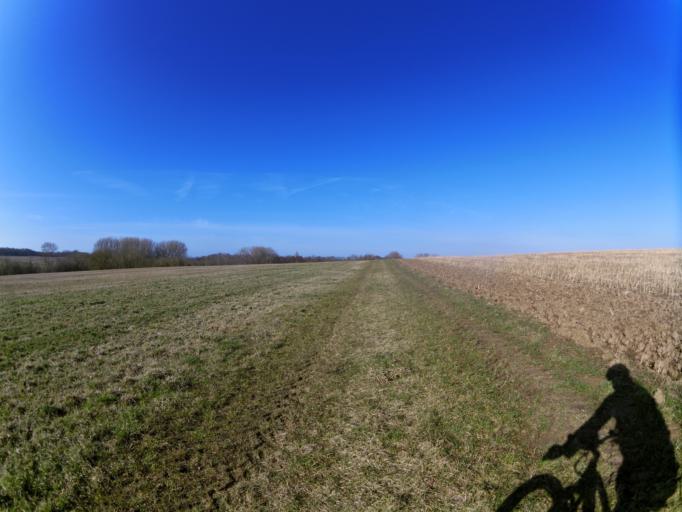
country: DE
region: Bavaria
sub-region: Regierungsbezirk Unterfranken
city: Eibelstadt
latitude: 49.6921
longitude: 9.9685
